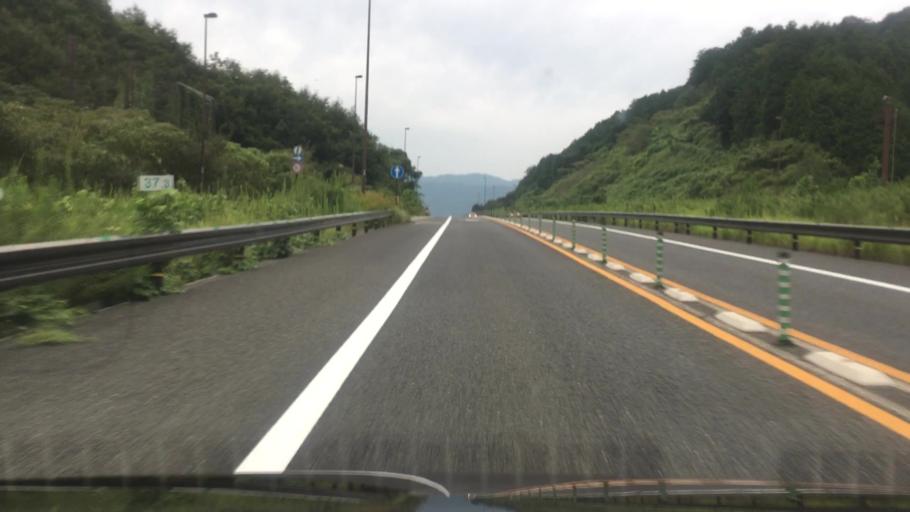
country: JP
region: Hyogo
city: Toyooka
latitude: 35.3102
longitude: 134.8688
